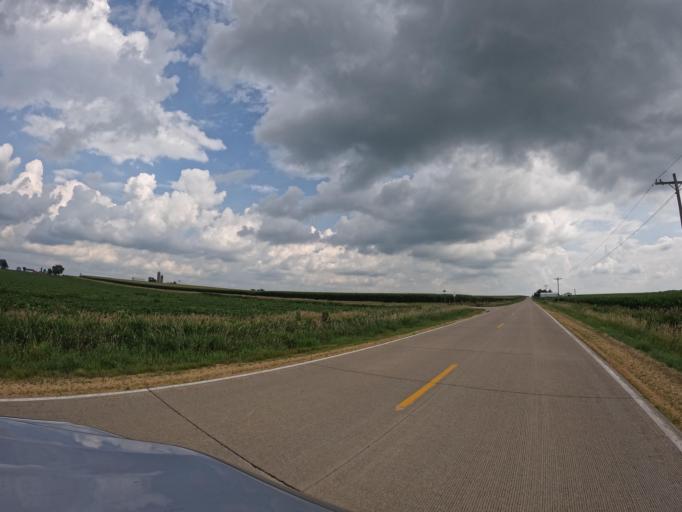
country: US
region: Iowa
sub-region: Clinton County
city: De Witt
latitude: 41.7798
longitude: -90.4133
